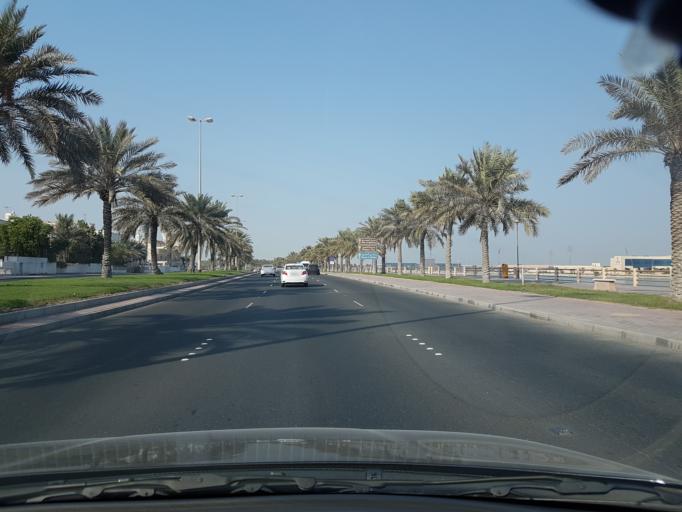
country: BH
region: Muharraq
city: Al Muharraq
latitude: 26.2512
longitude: 50.6210
